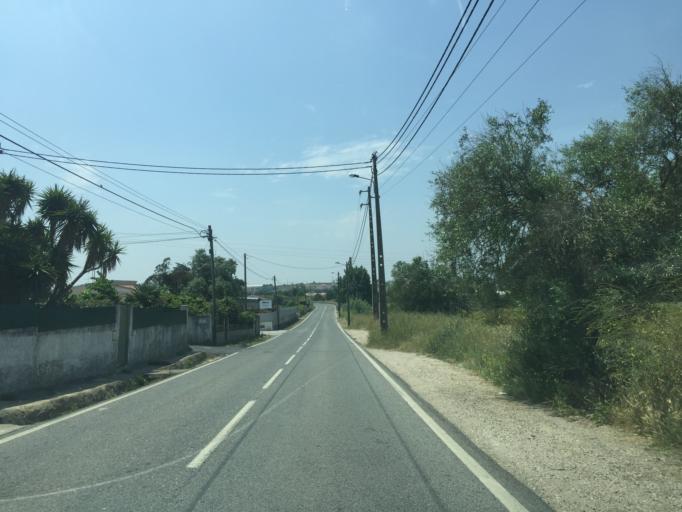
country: PT
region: Lisbon
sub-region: Mafra
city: Venda do Pinheiro
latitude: 38.8923
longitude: -9.1885
